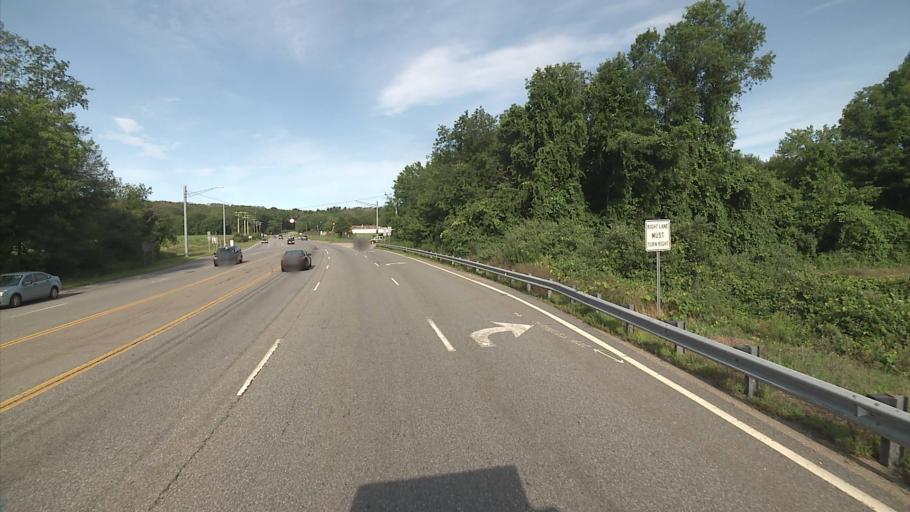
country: US
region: Connecticut
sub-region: New London County
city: Preston City
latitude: 41.4883
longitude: -71.9829
